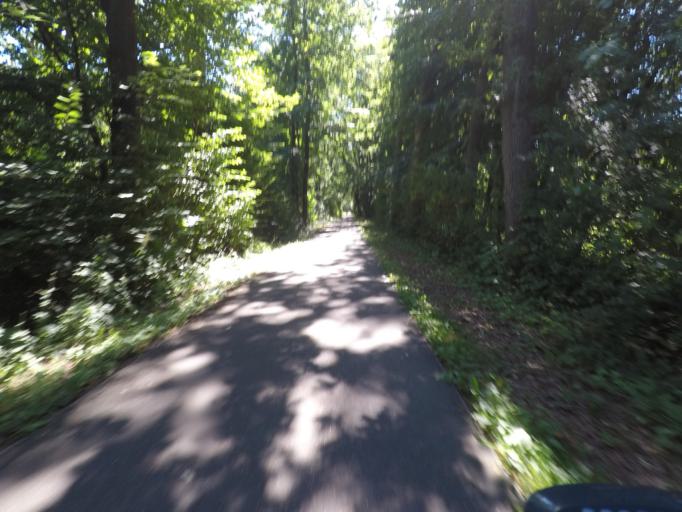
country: DE
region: Schleswig-Holstein
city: Trittau
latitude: 53.6323
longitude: 10.4001
